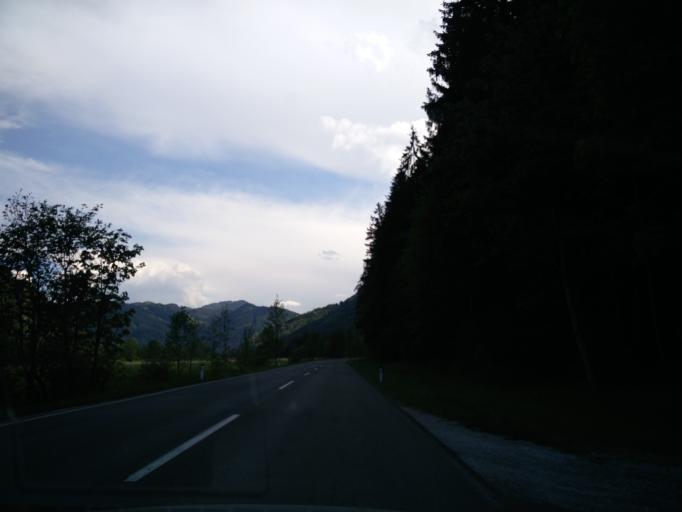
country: AT
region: Tyrol
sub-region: Politischer Bezirk Kitzbuhel
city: Kirchdorf in Tirol
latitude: 47.6079
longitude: 12.4679
